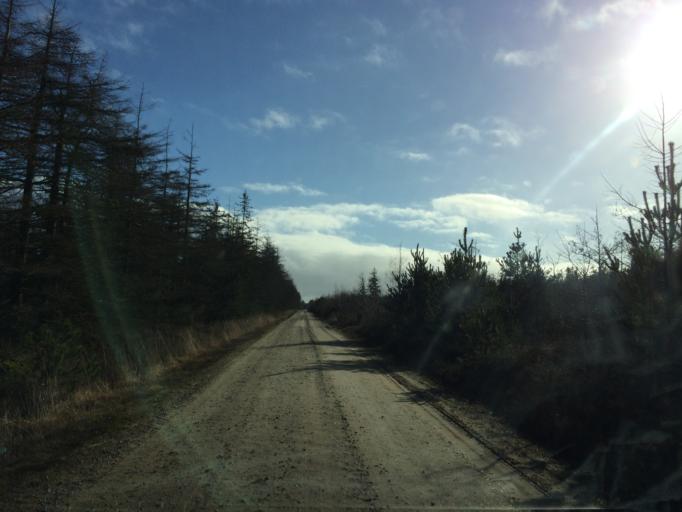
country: DK
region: Central Jutland
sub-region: Holstebro Kommune
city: Ulfborg
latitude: 56.2729
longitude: 8.3808
